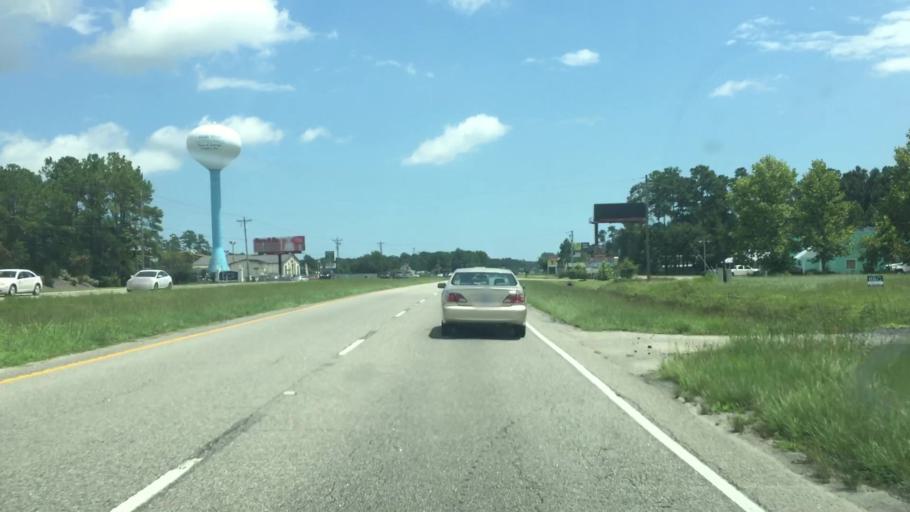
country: US
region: South Carolina
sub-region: Horry County
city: North Myrtle Beach
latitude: 33.9041
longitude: -78.7032
